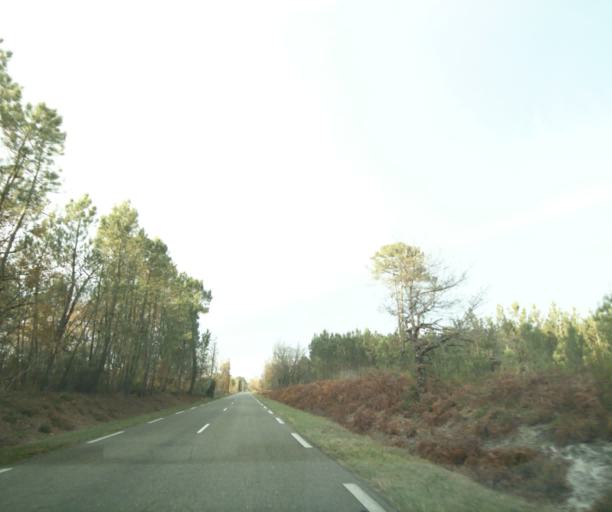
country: FR
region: Aquitaine
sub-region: Departement des Landes
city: Gabarret
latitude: 44.0500
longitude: -0.0419
